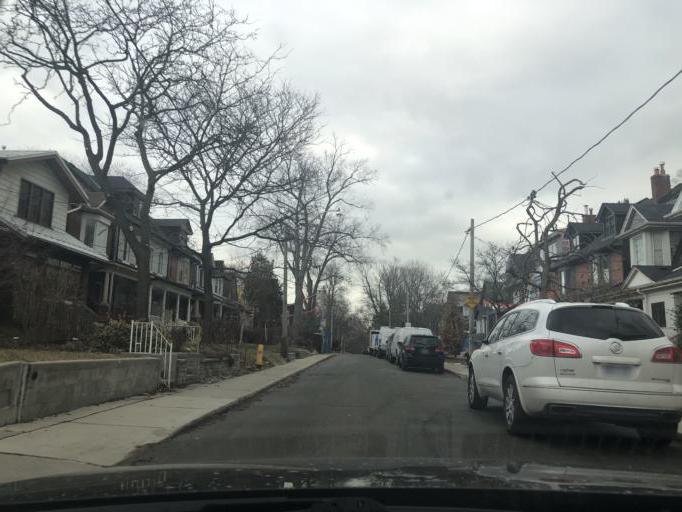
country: CA
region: Ontario
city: Toronto
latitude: 43.6736
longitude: -79.3507
